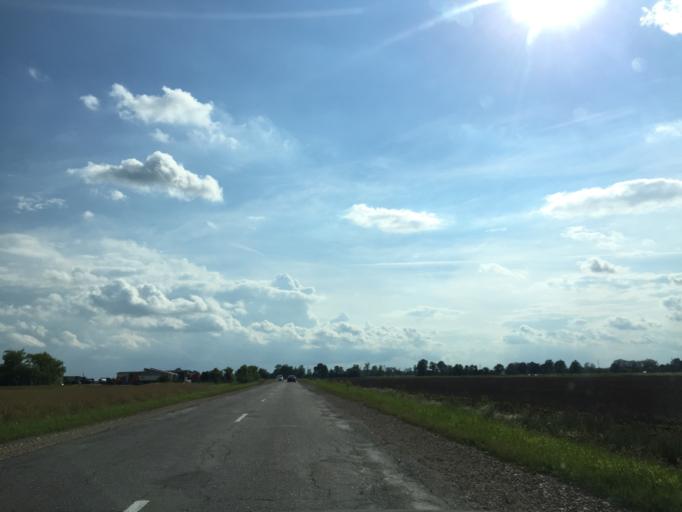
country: LV
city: Tervete
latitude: 56.5630
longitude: 23.4002
